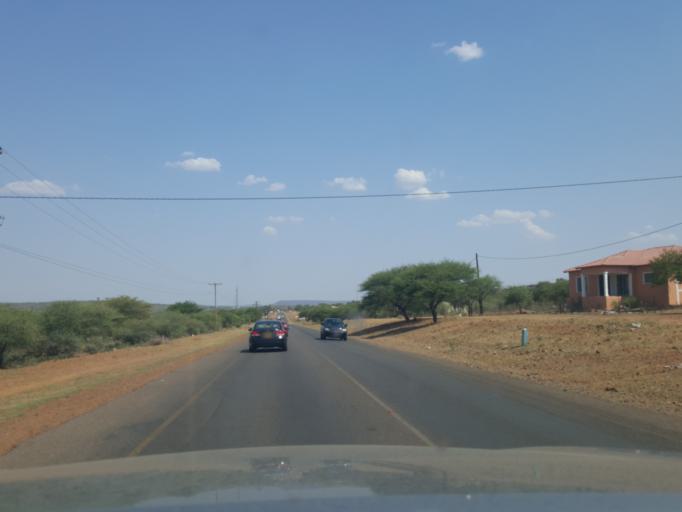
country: BW
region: South East
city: Ramotswa
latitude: -24.8370
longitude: 25.8189
